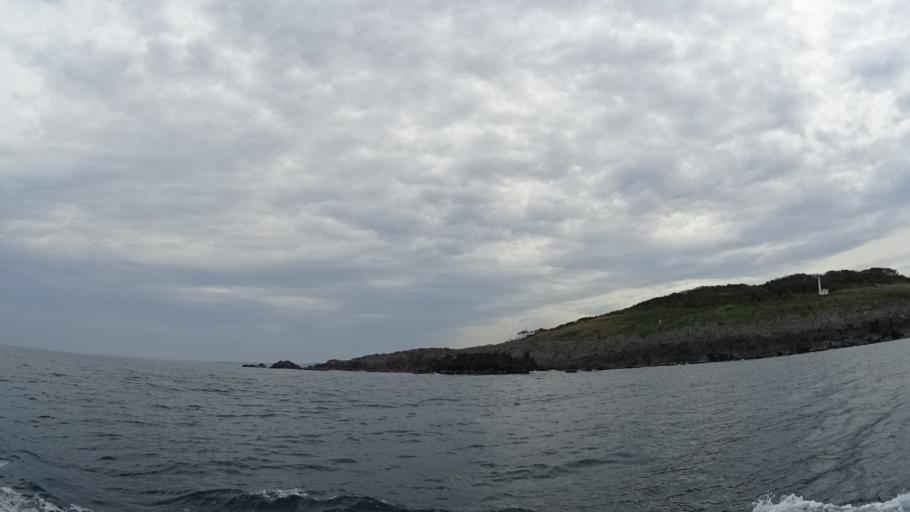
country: JP
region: Fukui
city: Mikuni
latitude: 36.2531
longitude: 136.1163
